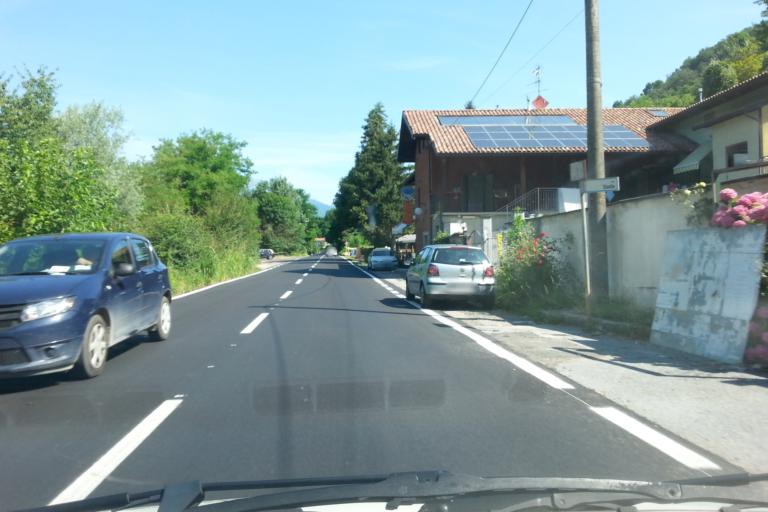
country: IT
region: Piedmont
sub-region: Provincia di Torino
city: Avigliana
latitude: 45.0542
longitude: 7.3965
